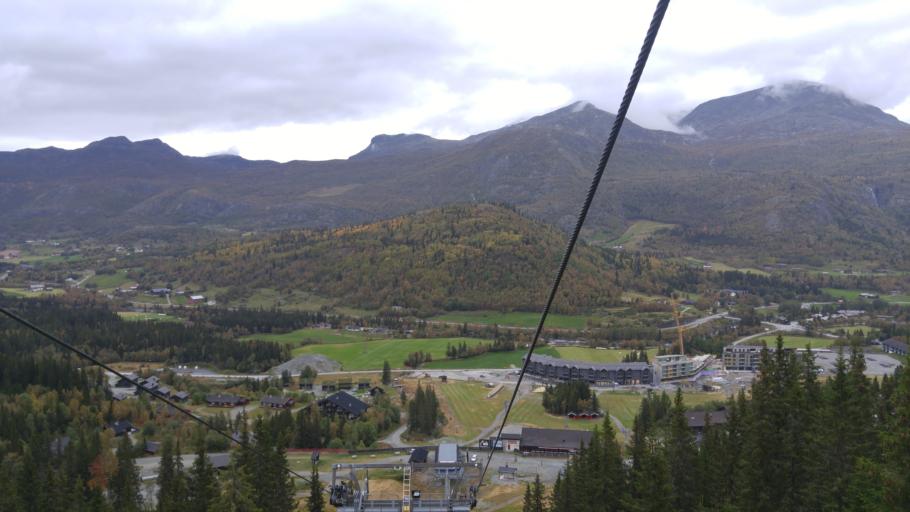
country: NO
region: Buskerud
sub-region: Hemsedal
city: Hemsedal
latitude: 60.8578
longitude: 8.5131
